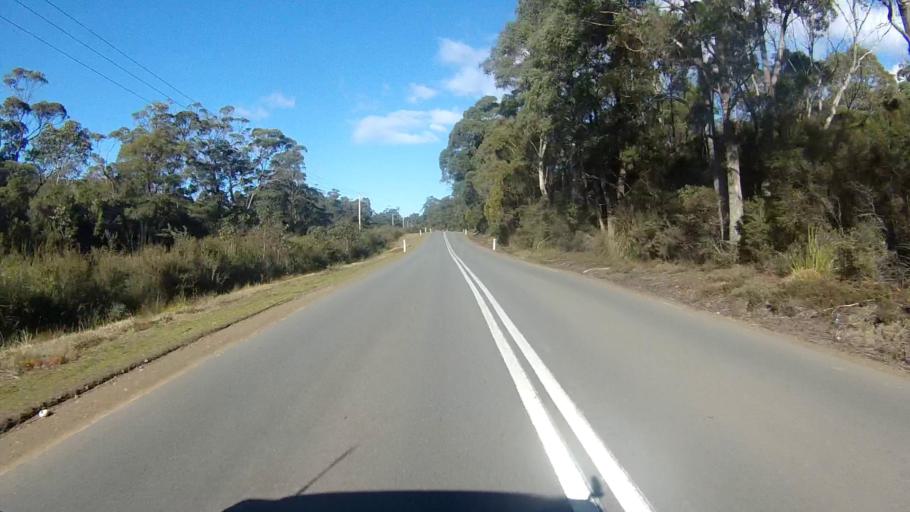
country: AU
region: Tasmania
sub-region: Clarence
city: Sandford
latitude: -43.0857
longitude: 147.8673
